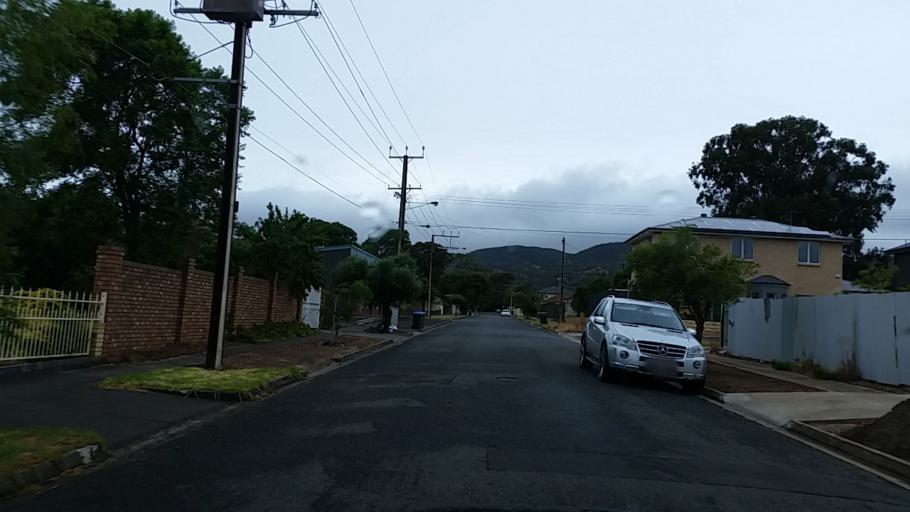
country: AU
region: South Australia
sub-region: Campbelltown
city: Campbelltown
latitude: -34.8972
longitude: 138.6793
